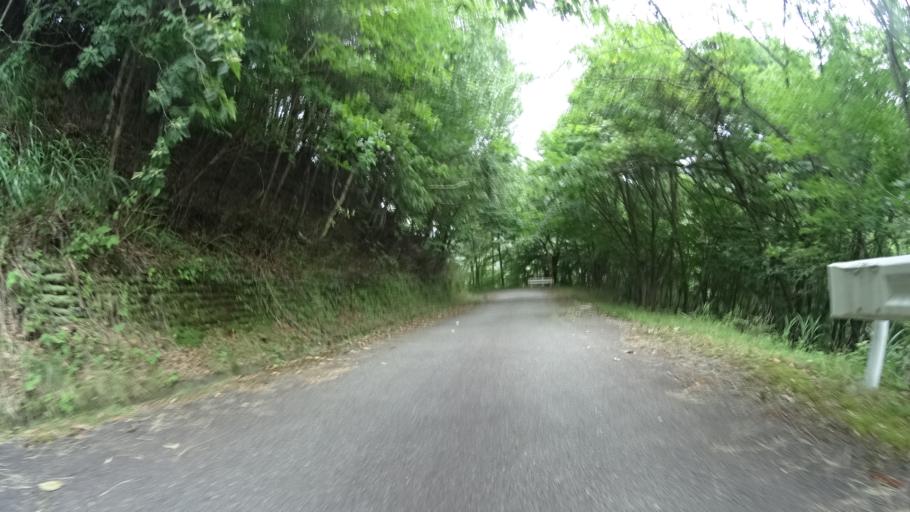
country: JP
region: Yamanashi
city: Kofu-shi
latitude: 35.8252
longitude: 138.5903
